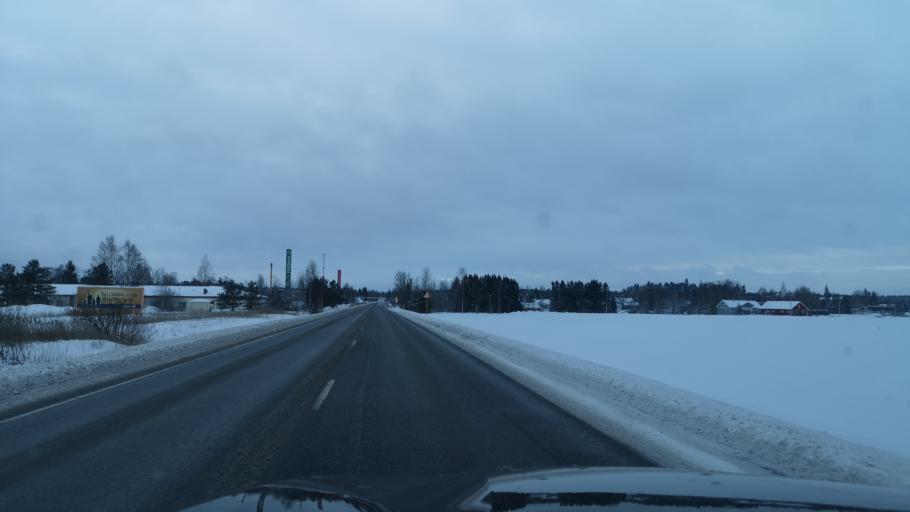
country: FI
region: Varsinais-Suomi
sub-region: Loimaa
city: Loimaa
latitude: 60.8608
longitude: 23.0470
